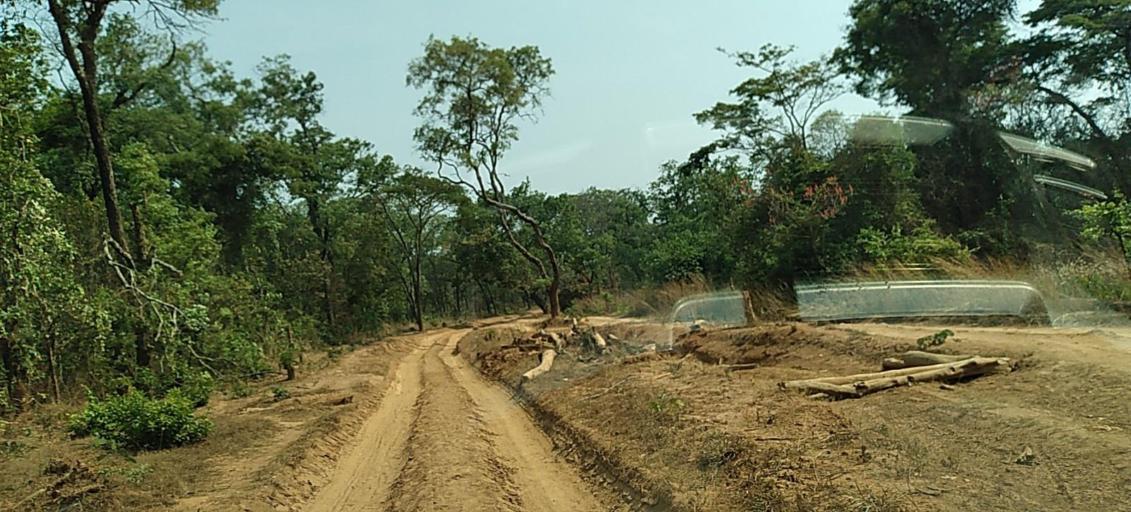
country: ZM
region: North-Western
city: Kansanshi
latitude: -12.0758
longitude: 26.8877
